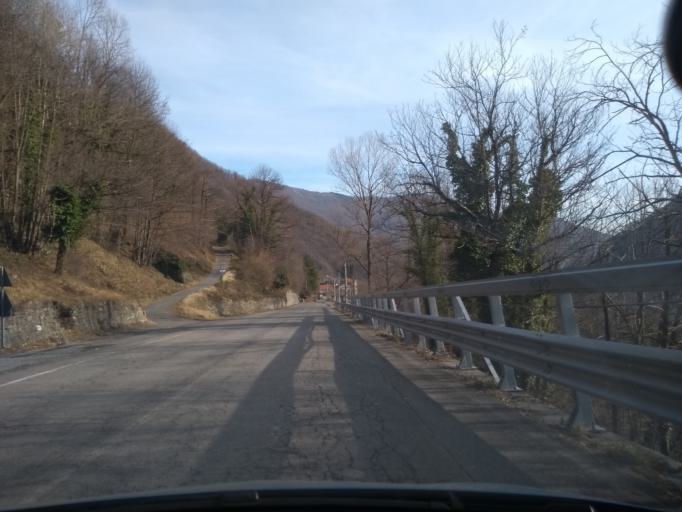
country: IT
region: Piedmont
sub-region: Provincia di Torino
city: Ceres
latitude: 45.3193
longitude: 7.3647
